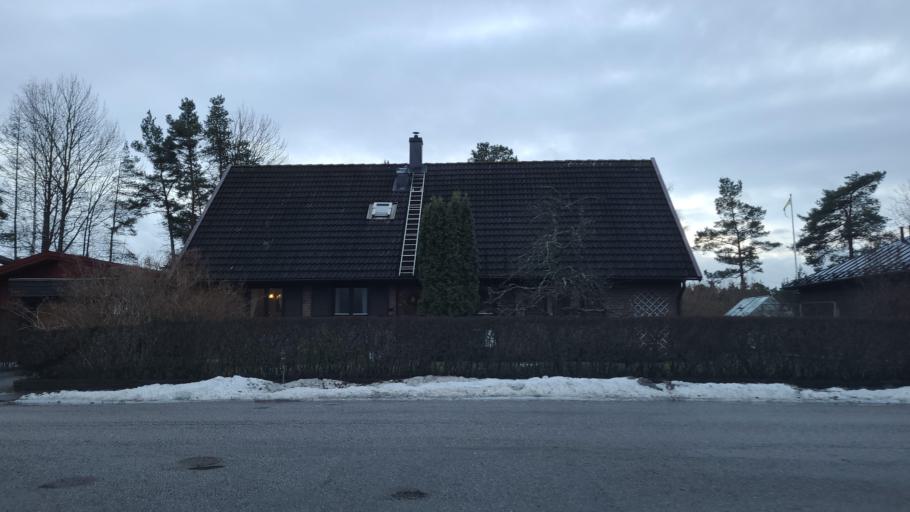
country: SE
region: Stockholm
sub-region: Vallentuna Kommun
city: Vallentuna
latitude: 59.5122
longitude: 18.0586
